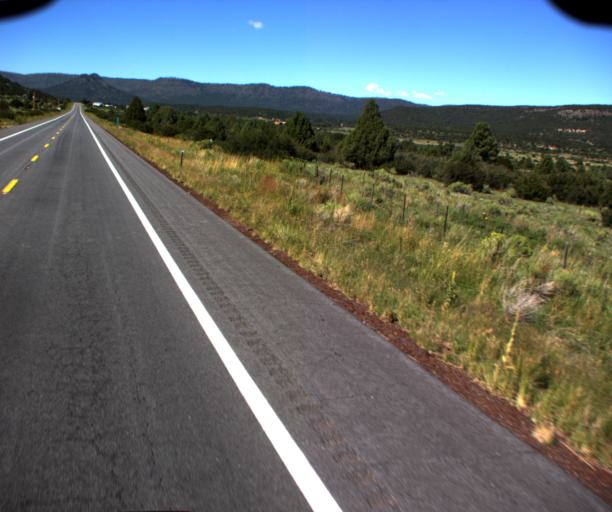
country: US
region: Arizona
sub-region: Apache County
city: Eagar
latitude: 33.9792
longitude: -109.1936
